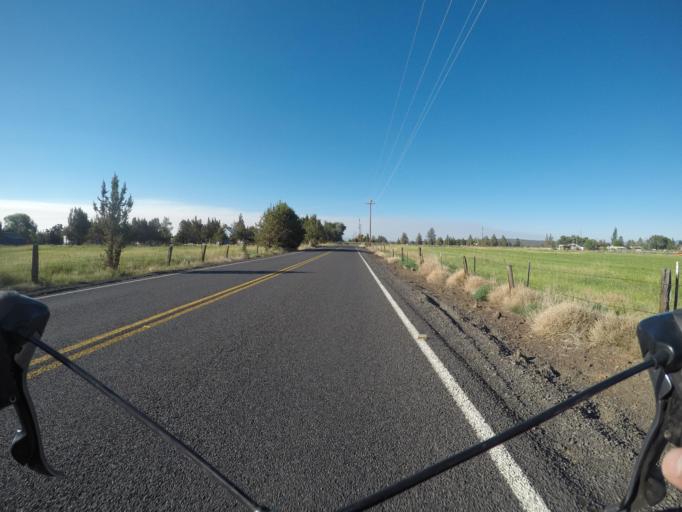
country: US
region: Oregon
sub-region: Deschutes County
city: Redmond
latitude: 44.2124
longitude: -121.2436
